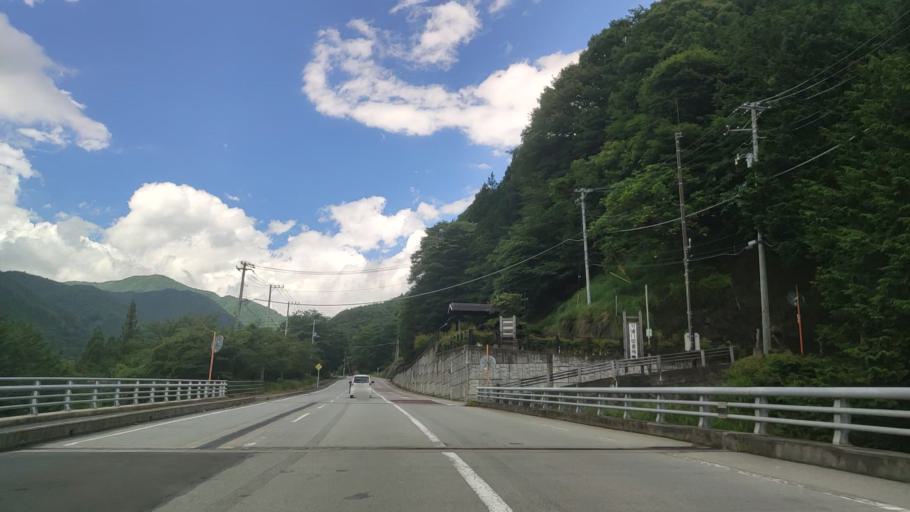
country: JP
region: Yamanashi
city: Enzan
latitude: 35.8027
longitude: 138.7499
